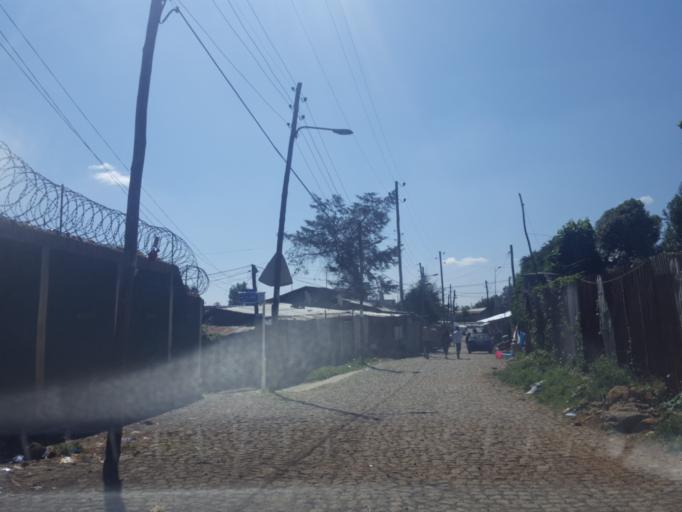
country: ET
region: Adis Abeba
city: Addis Ababa
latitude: 9.0482
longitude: 38.7690
